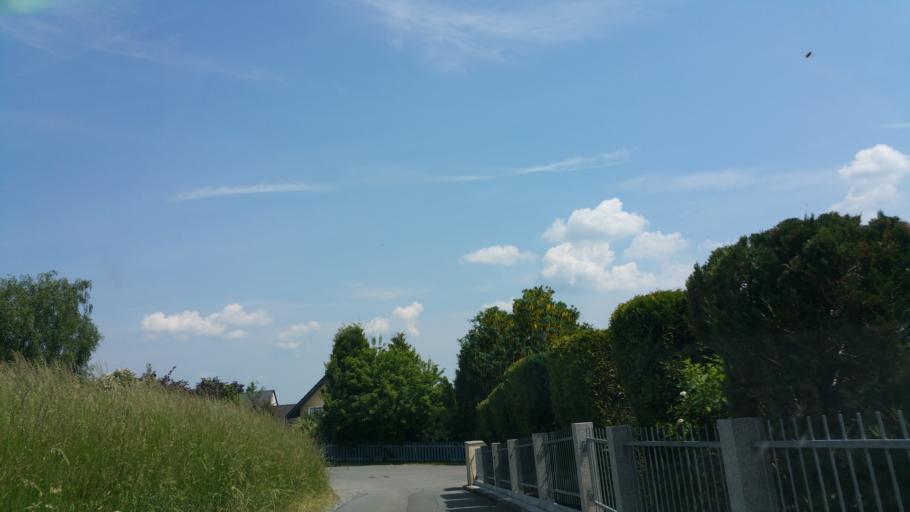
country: DE
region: Bavaria
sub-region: Upper Franconia
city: Schwarzenbach an der Saale
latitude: 50.2259
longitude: 11.9286
